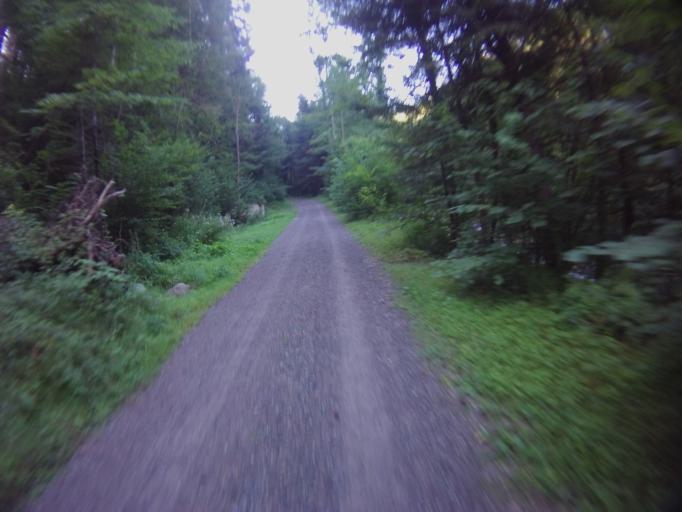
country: CH
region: Zug
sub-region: Zug
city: Menzingen
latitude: 47.1645
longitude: 8.5601
